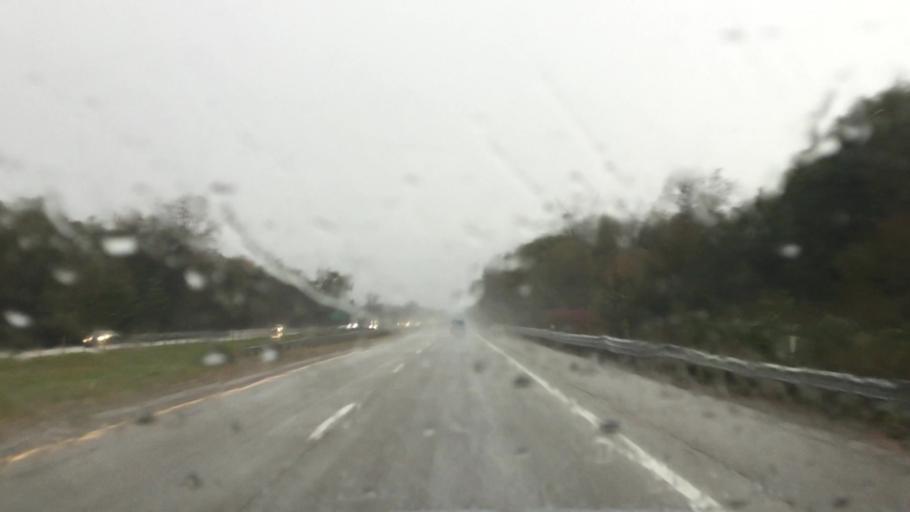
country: US
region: Michigan
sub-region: Van Buren County
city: Paw Paw
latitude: 42.2060
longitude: -85.9001
